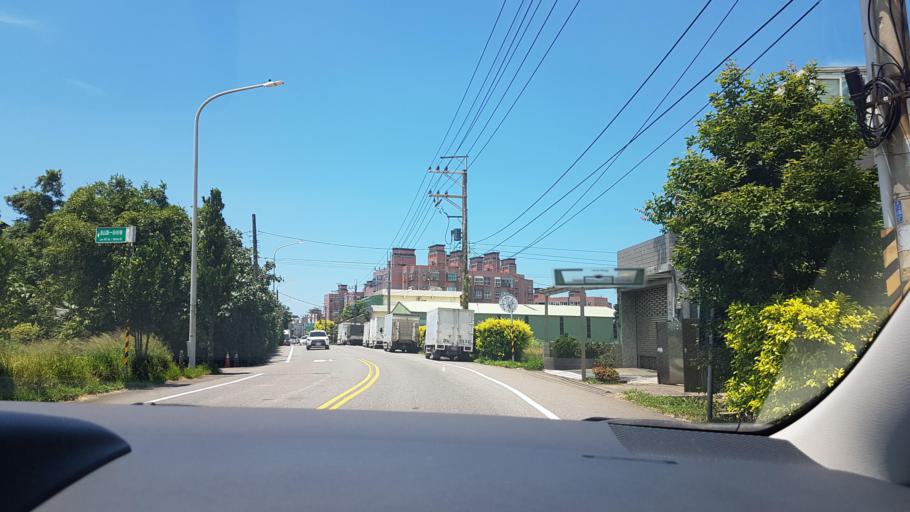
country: TW
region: Taiwan
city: Taoyuan City
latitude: 25.0985
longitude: 121.2630
